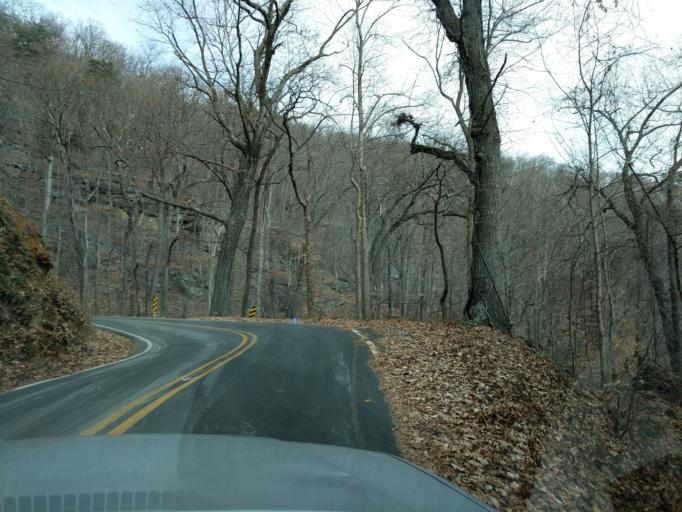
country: US
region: North Carolina
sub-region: Polk County
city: Columbus
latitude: 35.2636
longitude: -82.2323
